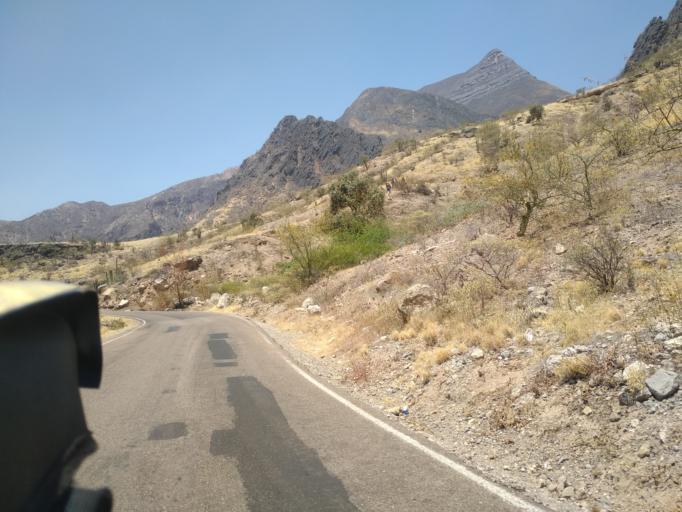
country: PE
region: Amazonas
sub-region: Provincia de Chachapoyas
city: Balsas
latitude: -6.8521
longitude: -78.0344
